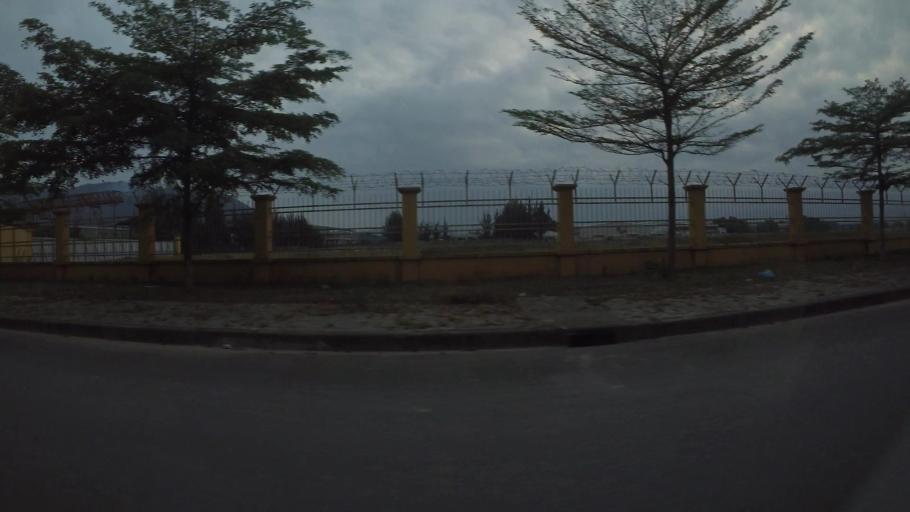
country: VN
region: Da Nang
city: Lien Chieu
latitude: 16.0837
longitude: 108.1167
